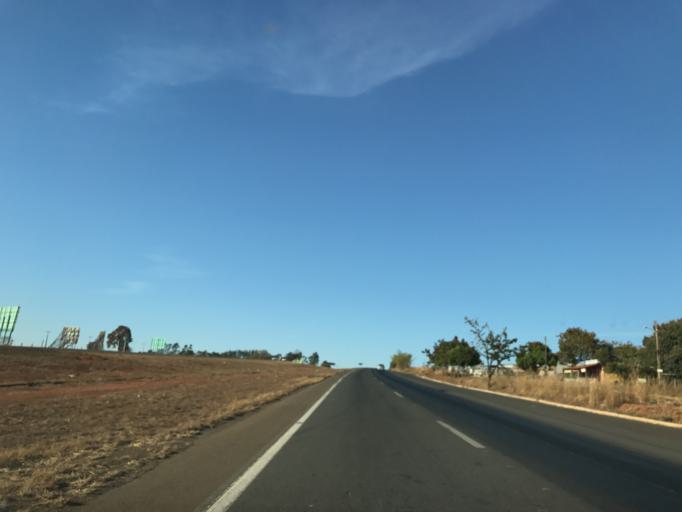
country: BR
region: Goias
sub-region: Aparecida De Goiania
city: Aparecida de Goiania
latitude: -16.8792
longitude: -49.2530
